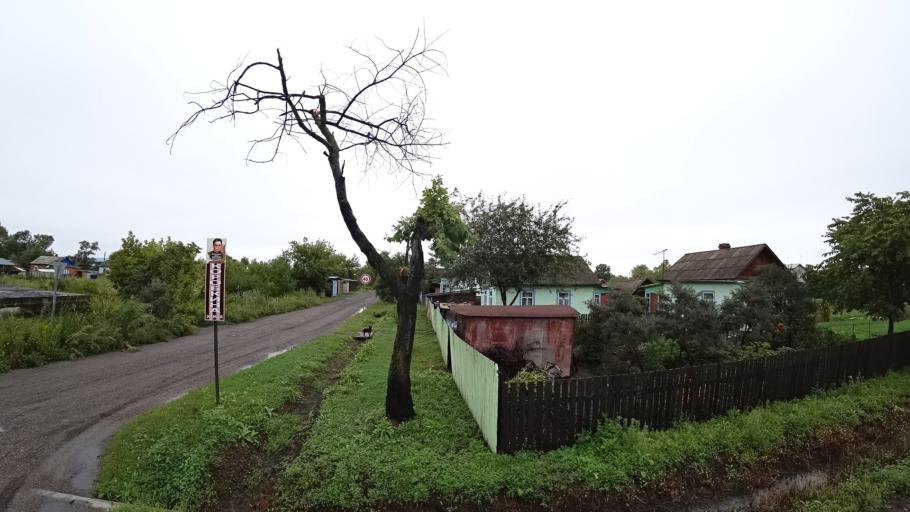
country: RU
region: Primorskiy
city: Monastyrishche
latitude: 44.1999
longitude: 132.4281
